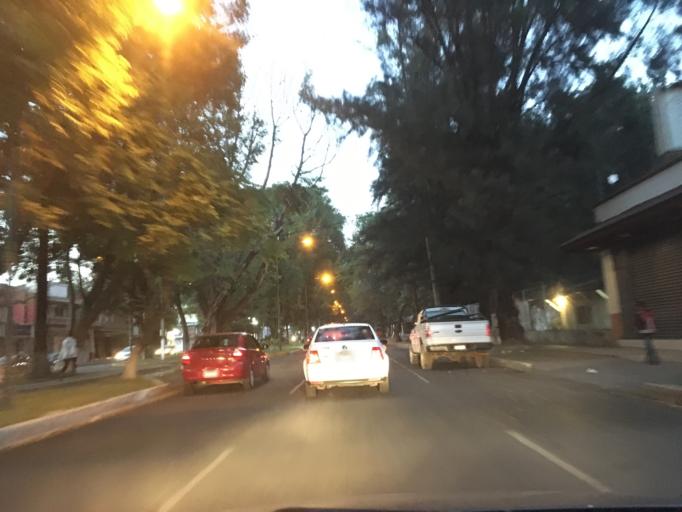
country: MX
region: Michoacan
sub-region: Uruapan
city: Uruapan
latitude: 19.4138
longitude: -102.0517
